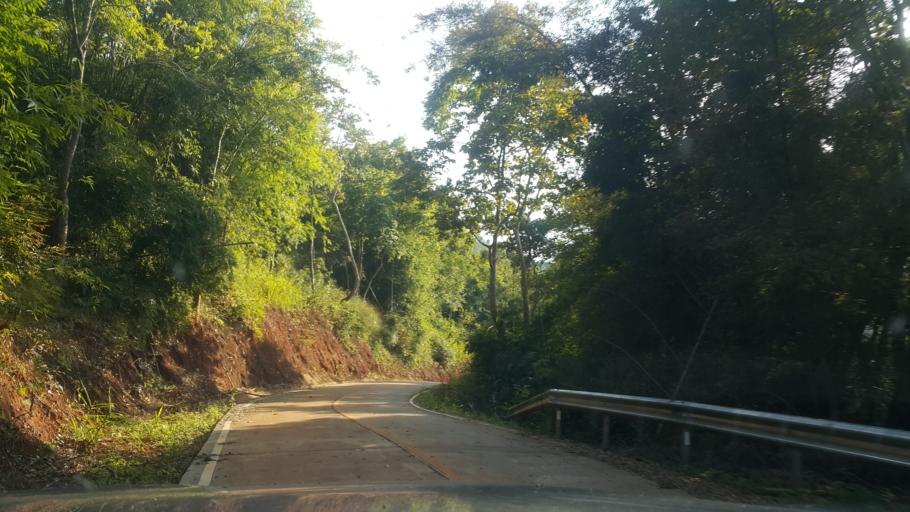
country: TH
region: Chiang Mai
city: Samoeng
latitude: 18.9979
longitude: 98.6800
